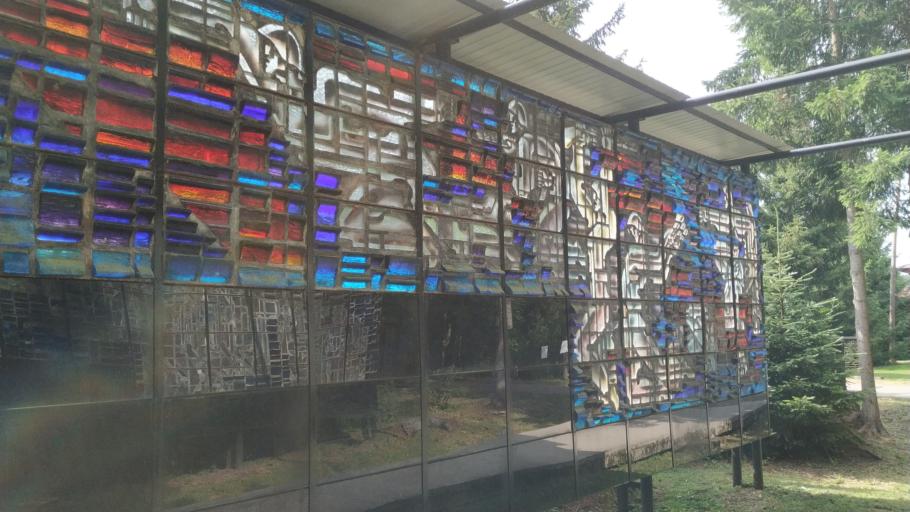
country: LT
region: Alytaus apskritis
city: Druskininkai
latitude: 54.0217
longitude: 24.0807
